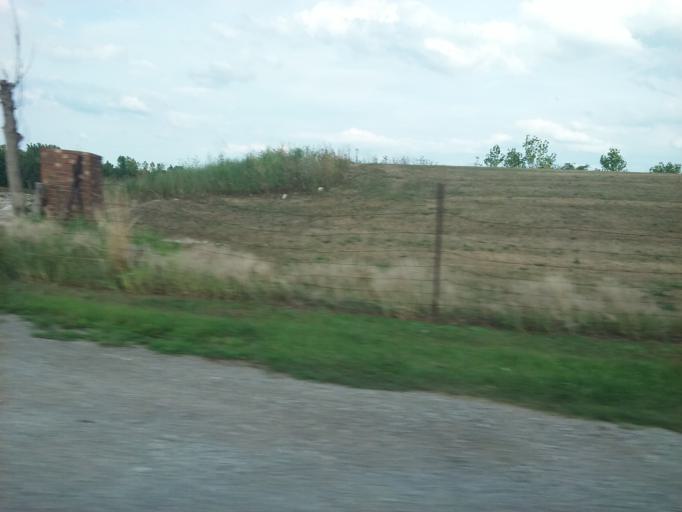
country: US
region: Ohio
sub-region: Wood County
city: Bowling Green
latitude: 41.3201
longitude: -83.6503
